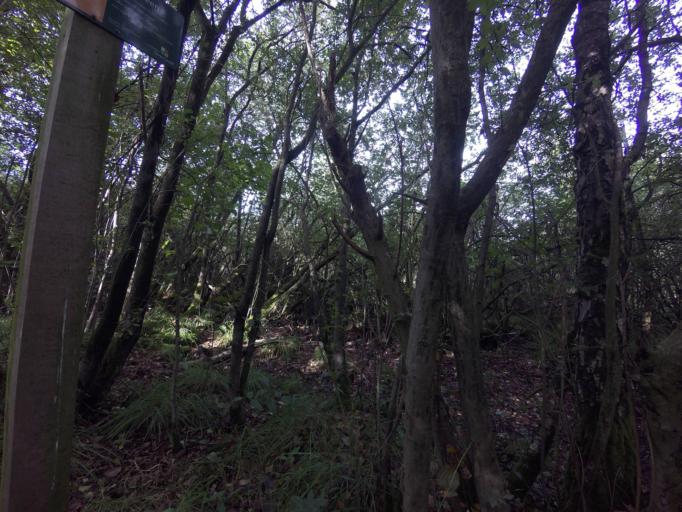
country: DE
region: North Rhine-Westphalia
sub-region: Regierungsbezirk Munster
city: Gronau
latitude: 52.1885
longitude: 6.9596
